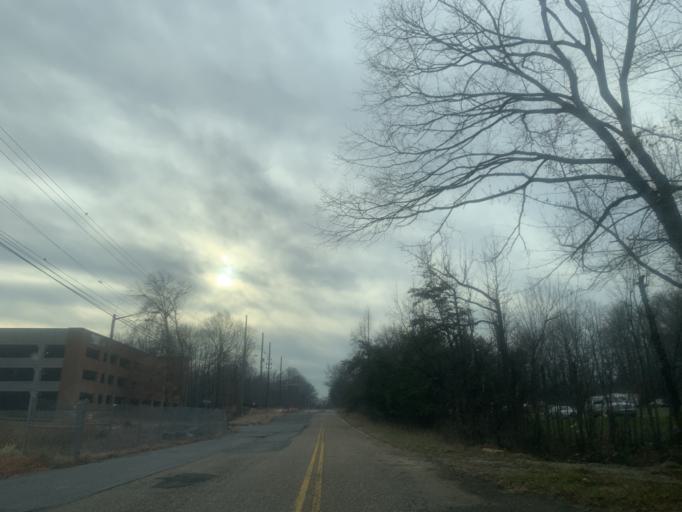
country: US
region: Maryland
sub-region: Prince George's County
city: Forestville
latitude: 38.8271
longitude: -76.8539
